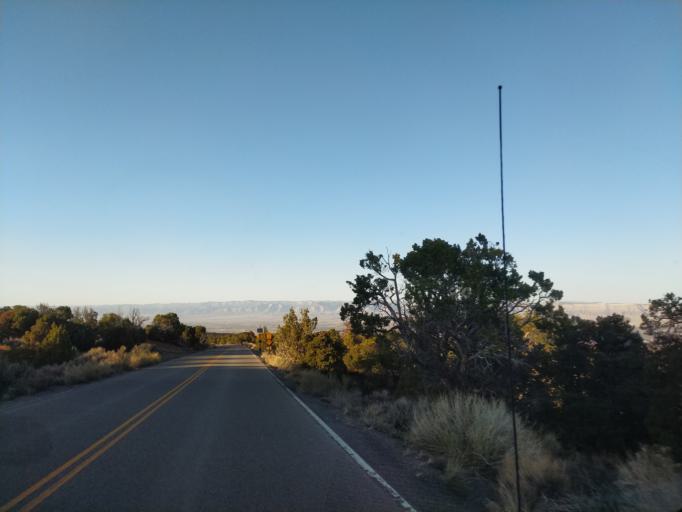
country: US
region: Colorado
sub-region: Mesa County
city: Redlands
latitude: 39.0199
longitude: -108.6597
